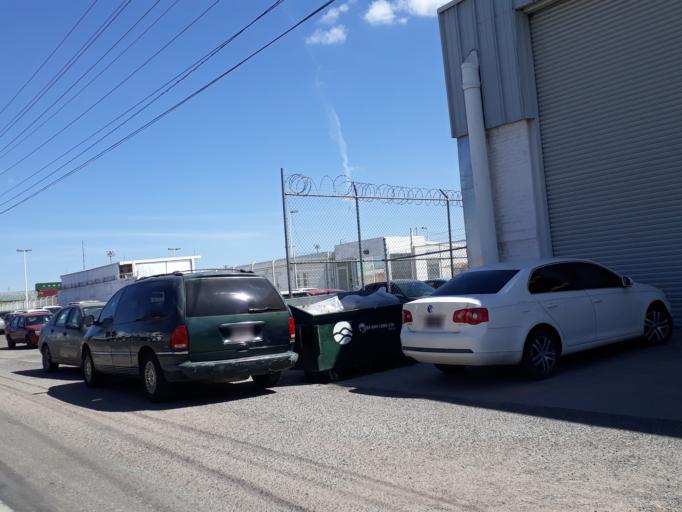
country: MX
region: Aguascalientes
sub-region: Aguascalientes
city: San Sebastian [Fraccionamiento]
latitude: 21.7980
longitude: -102.2801
